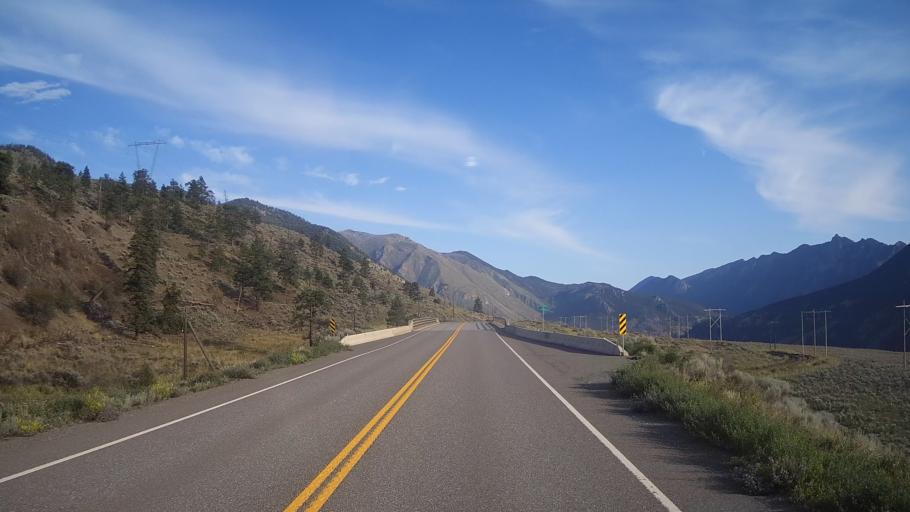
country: CA
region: British Columbia
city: Lillooet
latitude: 50.8128
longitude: -121.8498
